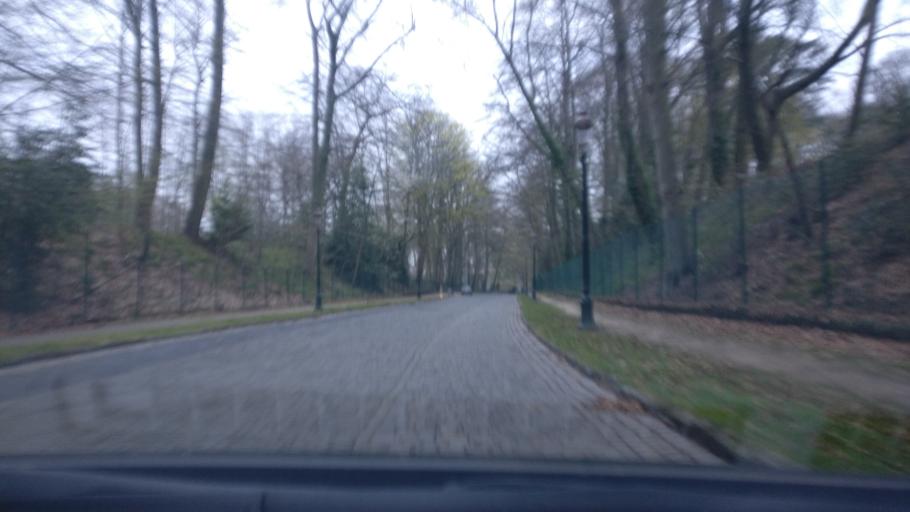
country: BE
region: Flanders
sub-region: Provincie Vlaams-Brabant
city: Kraainem
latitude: 50.8187
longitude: 4.4358
